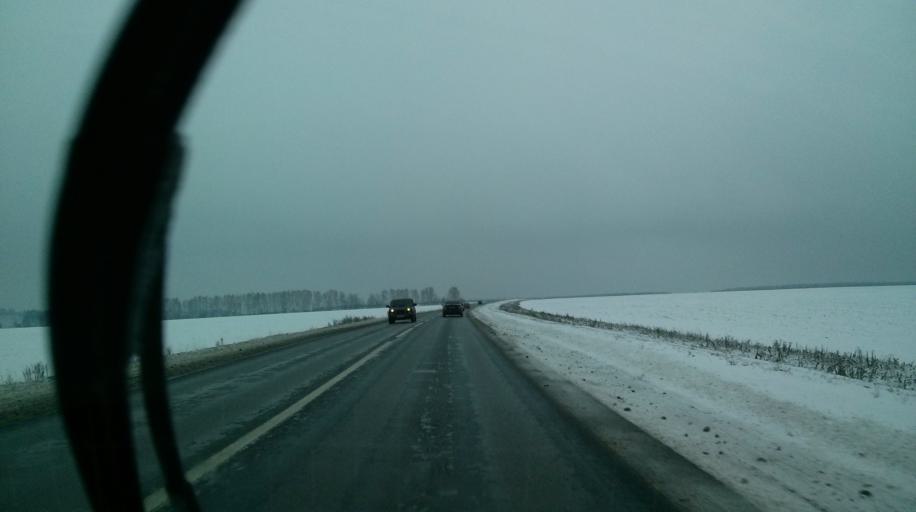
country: RU
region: Nizjnij Novgorod
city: Bogorodsk
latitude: 56.0963
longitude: 43.5812
